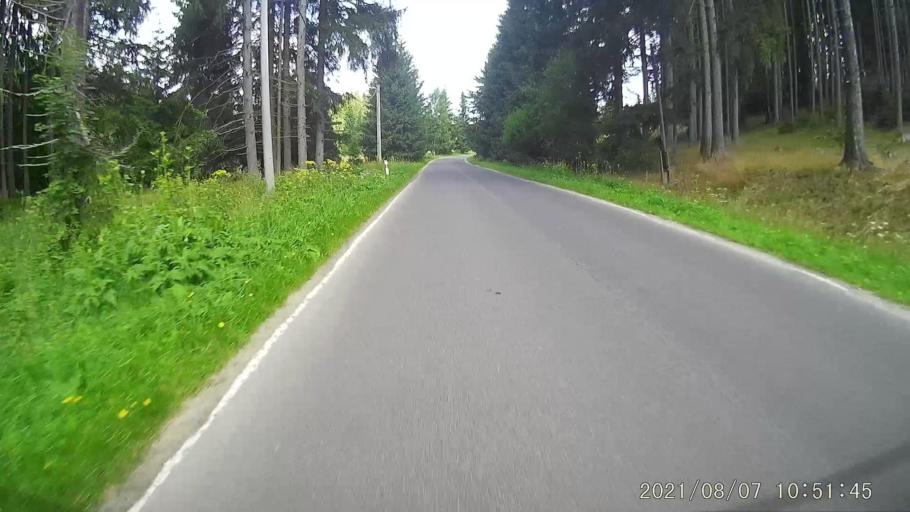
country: CZ
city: Rokytnice v Orlickych Horach
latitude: 50.2865
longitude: 16.4685
